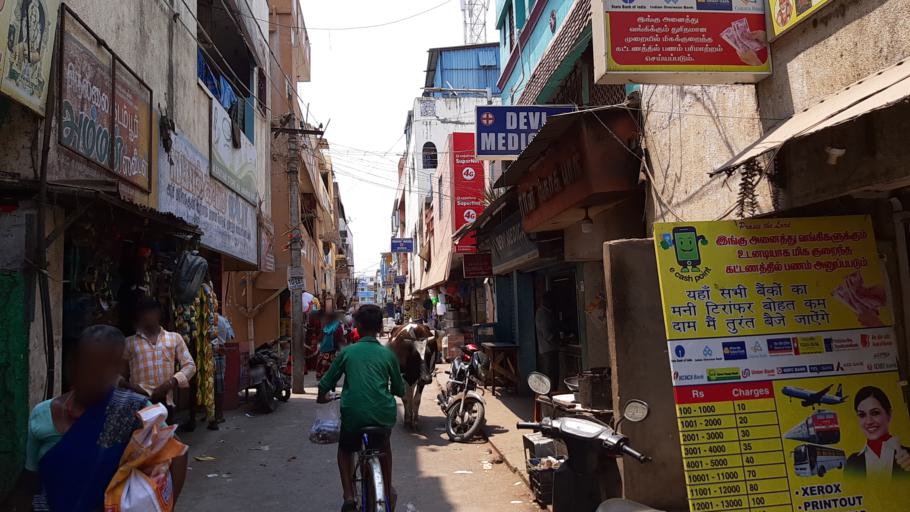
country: IN
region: Tamil Nadu
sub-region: Chennai
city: Chetput
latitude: 13.0701
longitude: 80.1975
